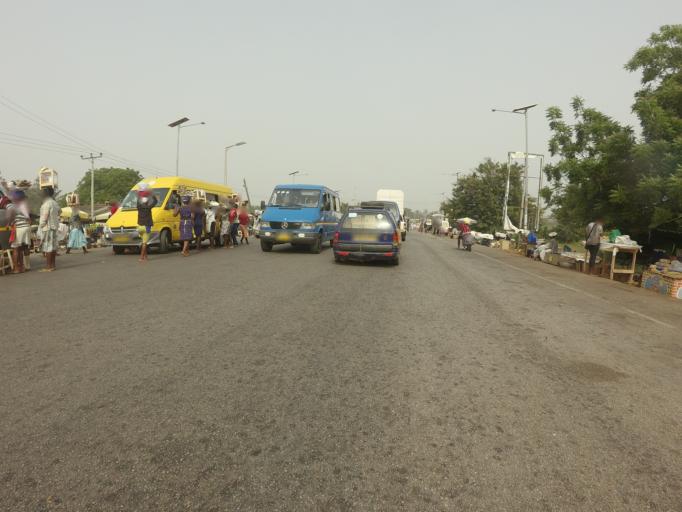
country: GH
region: Volta
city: Anloga
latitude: 5.9967
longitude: 0.5879
